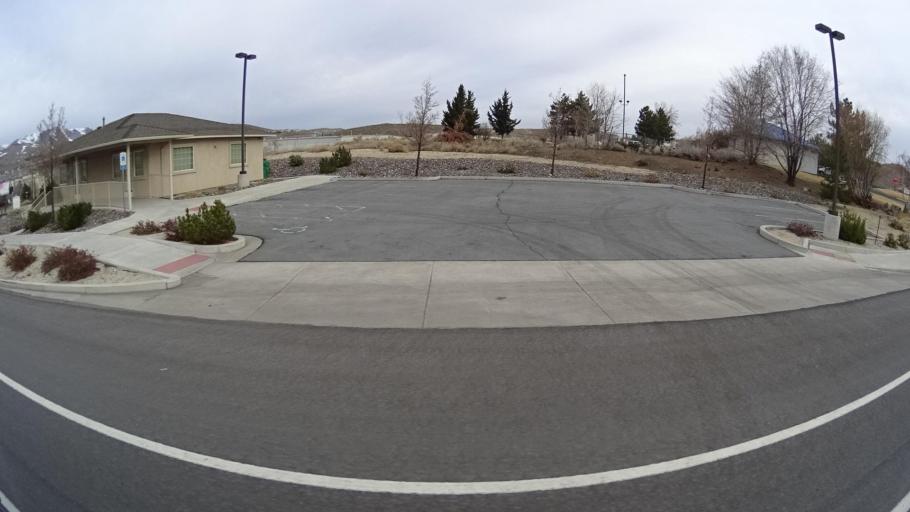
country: US
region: Nevada
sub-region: Washoe County
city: Reno
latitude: 39.5709
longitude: -119.8111
